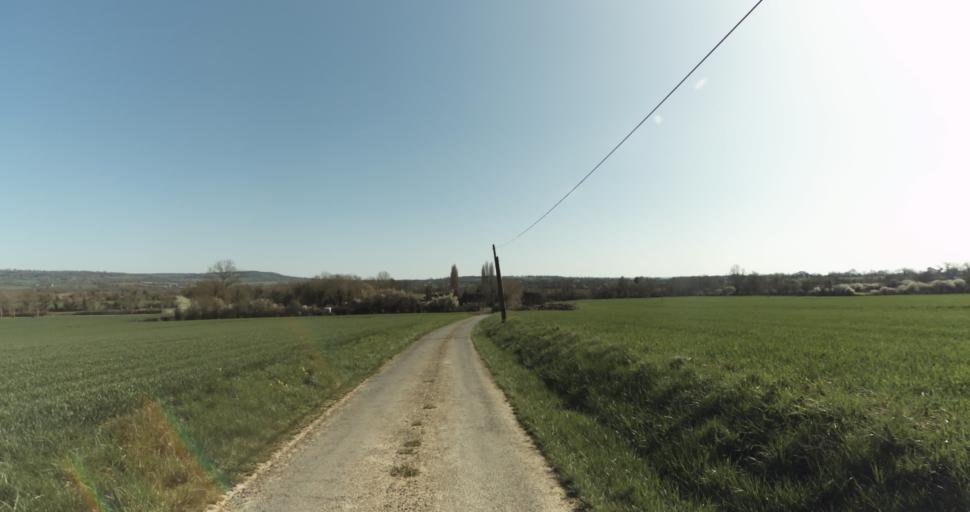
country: FR
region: Lower Normandy
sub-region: Departement du Calvados
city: Saint-Pierre-sur-Dives
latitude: 48.9384
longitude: 0.0024
